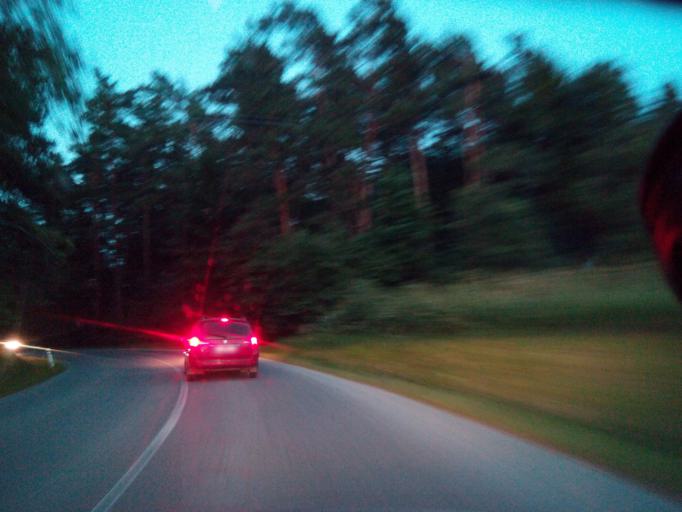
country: SK
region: Presovsky
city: Spisske Podhradie
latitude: 48.9419
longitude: 20.7312
